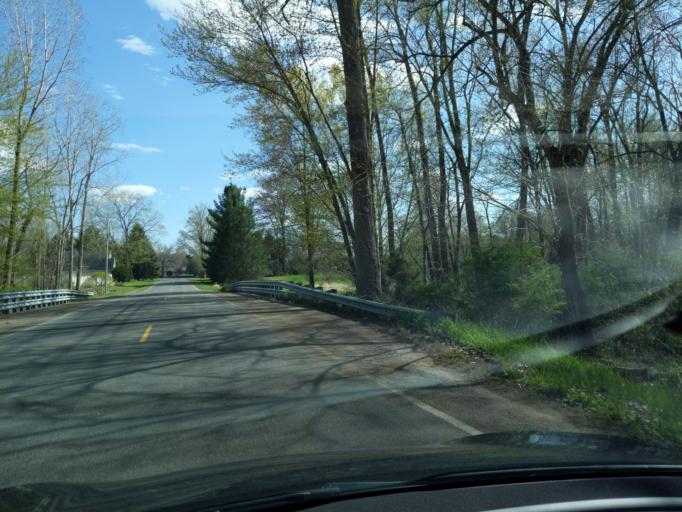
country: US
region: Michigan
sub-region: Ingham County
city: Leslie
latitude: 42.3751
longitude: -84.5417
